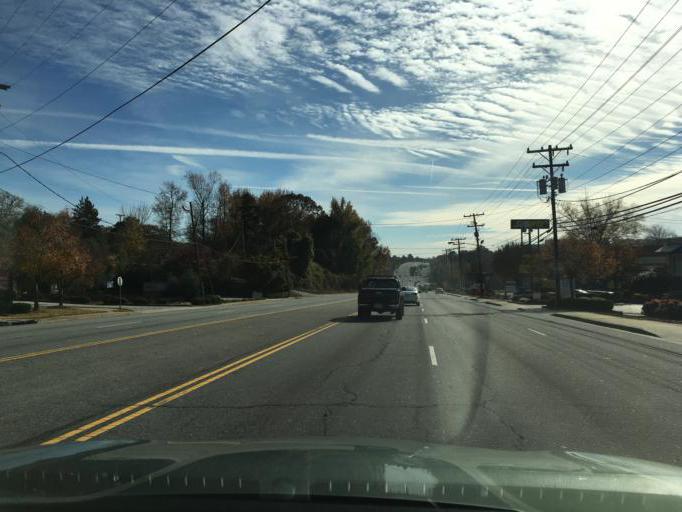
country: US
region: South Carolina
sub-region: Greenville County
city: Greenville
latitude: 34.8661
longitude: -82.3578
